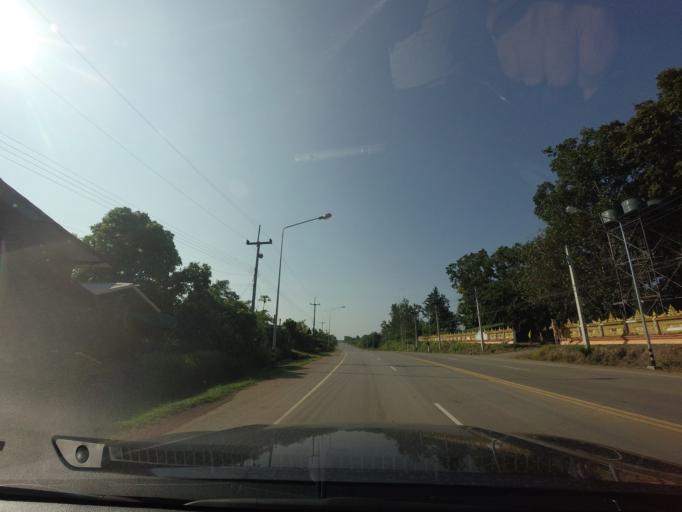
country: TH
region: Phetchabun
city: Lom Kao
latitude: 16.8317
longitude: 101.1807
